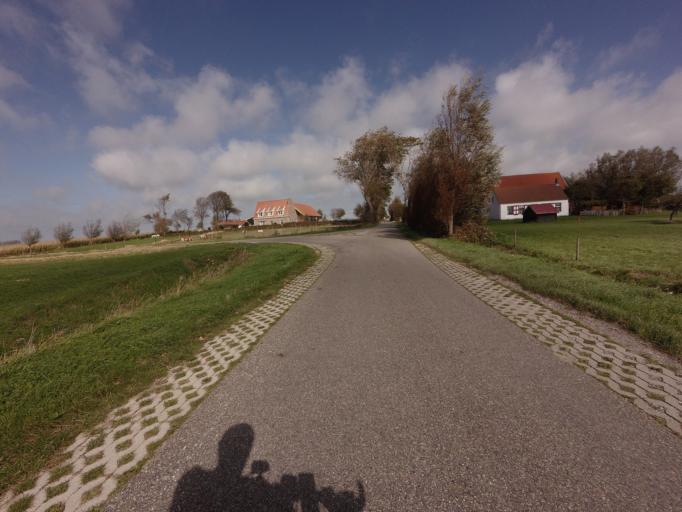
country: NL
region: Zeeland
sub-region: Gemeente Middelburg
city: Middelburg
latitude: 51.5347
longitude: 3.5247
